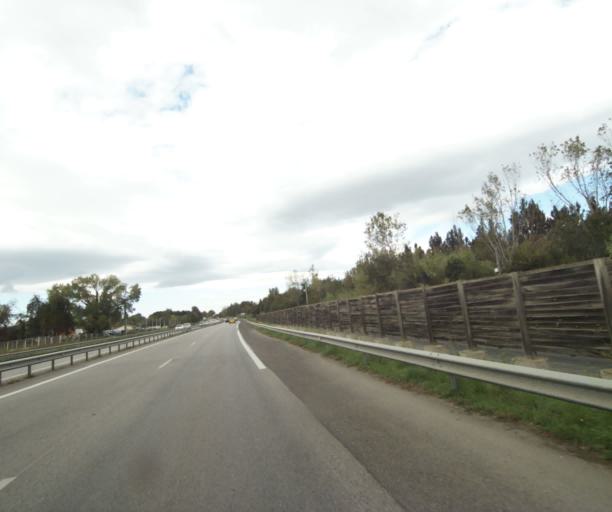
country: FR
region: Languedoc-Roussillon
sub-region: Departement des Pyrenees-Orientales
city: Sant Andreu de Sureda
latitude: 42.5721
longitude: 2.9976
